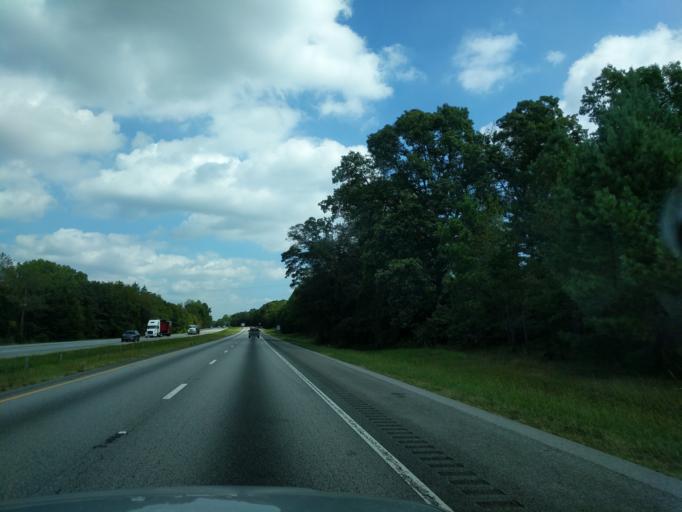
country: US
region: Georgia
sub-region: Hart County
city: Reed Creek
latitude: 34.5272
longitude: -82.8430
